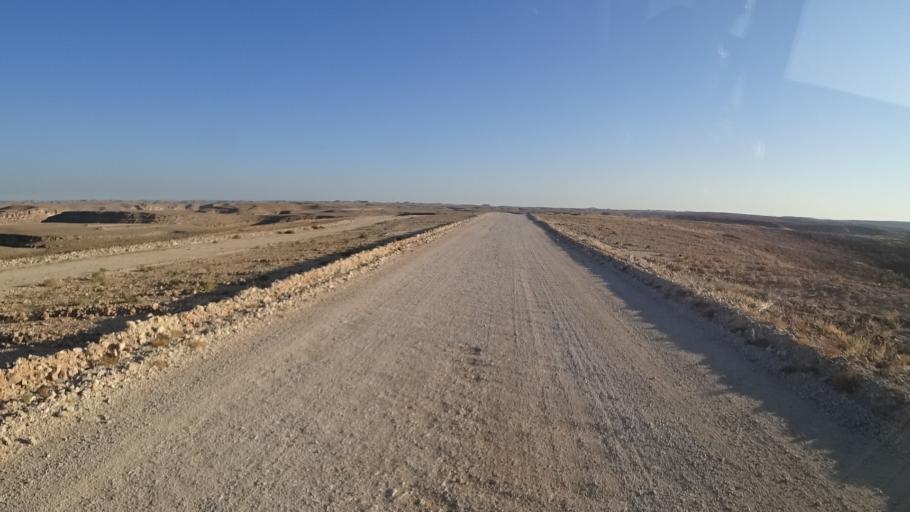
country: YE
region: Al Mahrah
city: Hawf
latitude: 17.1960
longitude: 53.3388
